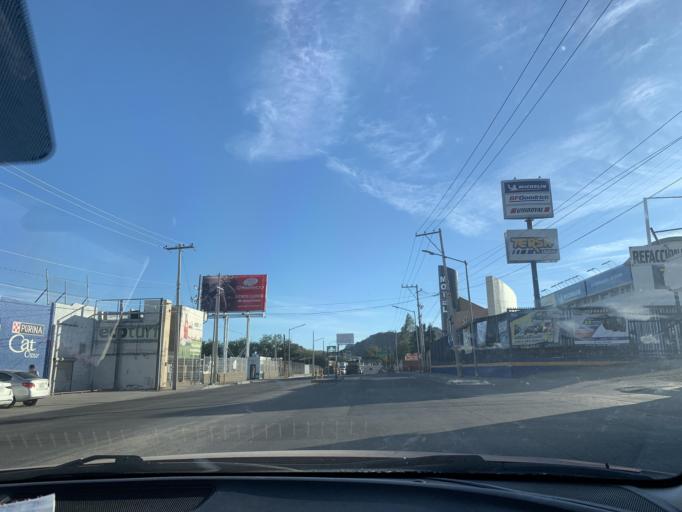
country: MX
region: Sonora
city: Hermosillo
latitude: 29.0945
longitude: -110.9311
